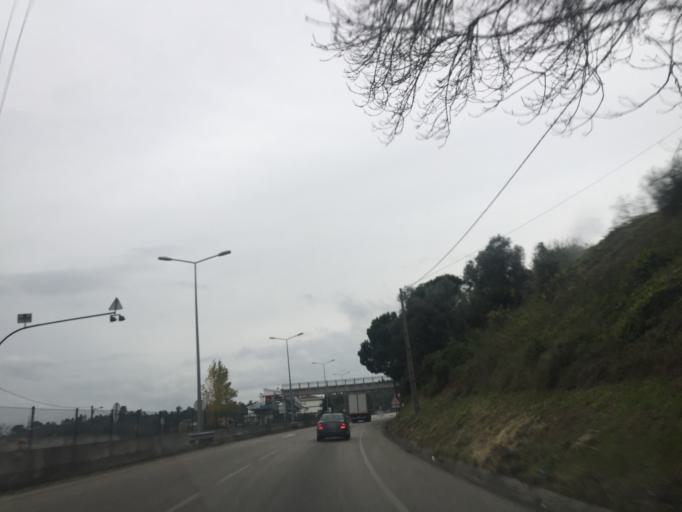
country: PT
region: Coimbra
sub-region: Coimbra
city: Coimbra
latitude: 40.1866
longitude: -8.4299
